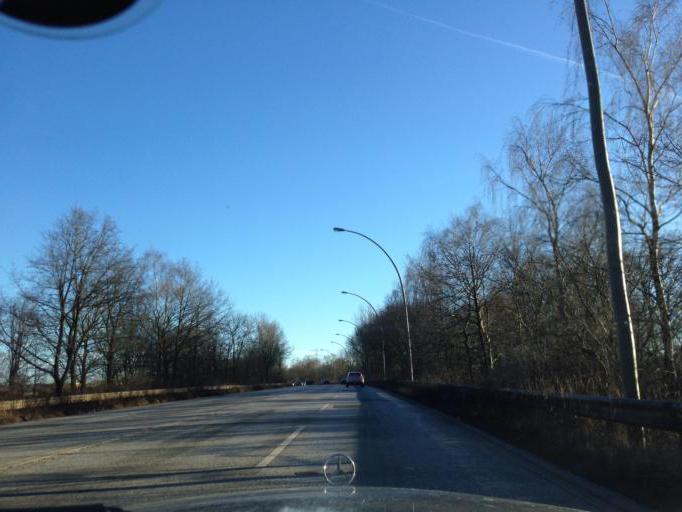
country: DE
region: Schleswig-Holstein
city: Stapelfeld
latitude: 53.6123
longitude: 10.1771
